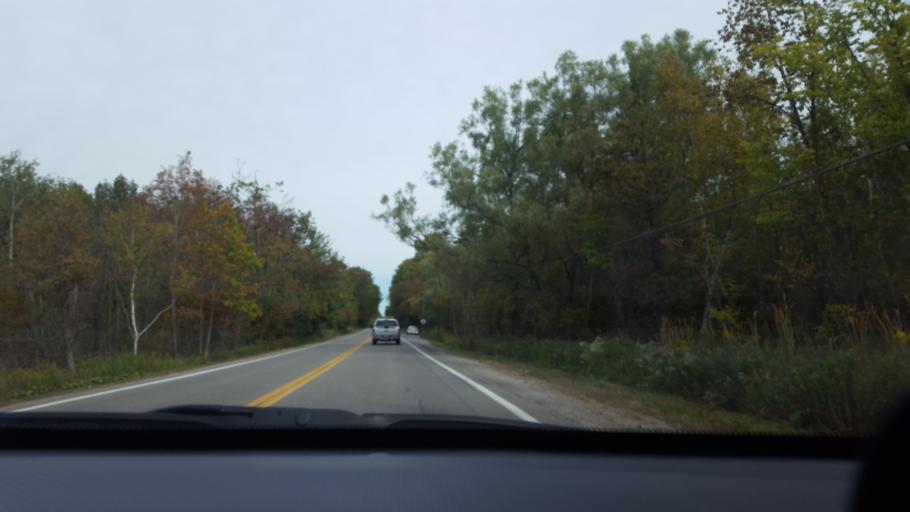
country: CA
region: Ontario
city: Newmarket
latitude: 43.9531
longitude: -79.5349
